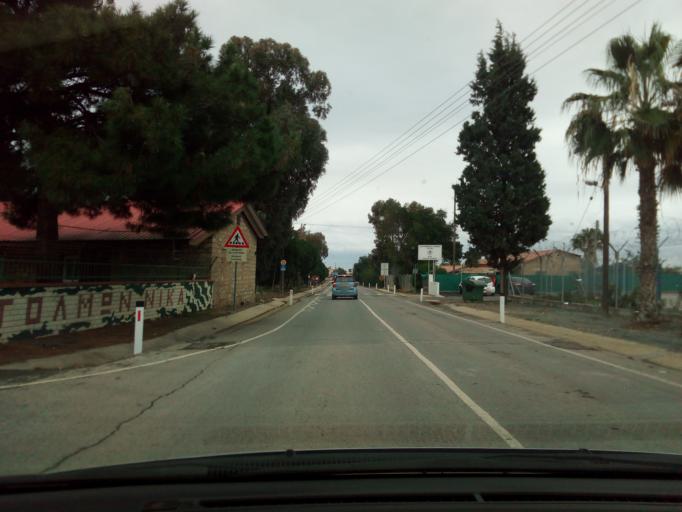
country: CY
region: Larnaka
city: Kofinou
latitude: 34.7327
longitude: 33.3352
